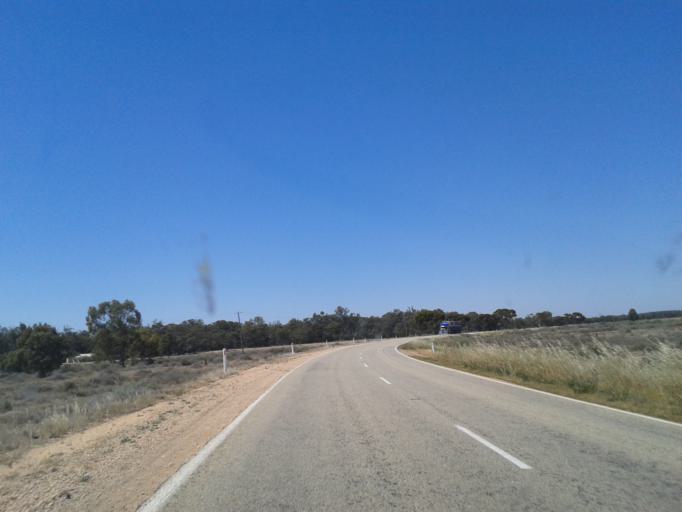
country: AU
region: Victoria
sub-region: Swan Hill
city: Swan Hill
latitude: -34.7591
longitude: 143.2172
